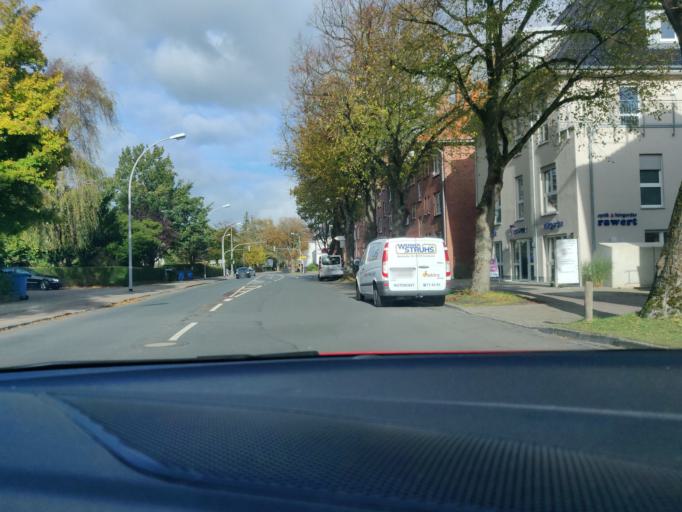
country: DE
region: Lower Saxony
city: Cuxhaven
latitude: 53.8578
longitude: 8.6935
